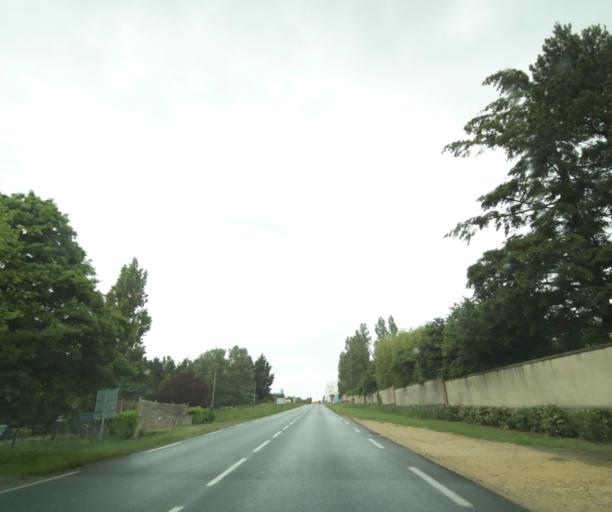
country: FR
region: Poitou-Charentes
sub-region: Departement des Deux-Sevres
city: Chatillon-sur-Thouet
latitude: 46.6670
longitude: -0.2471
